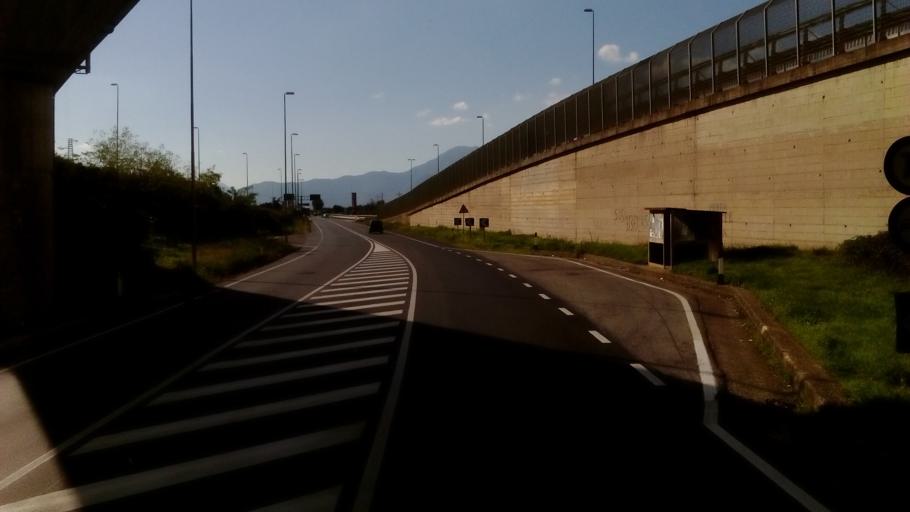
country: IT
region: Molise
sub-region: Provincia di Isernia
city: Taverna Ravindola
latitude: 41.5172
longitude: 14.1257
